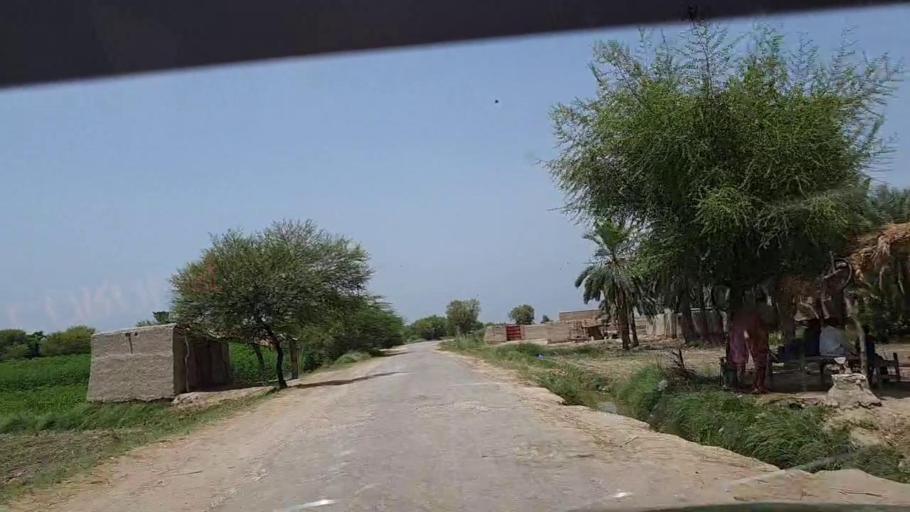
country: PK
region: Sindh
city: Khanpur
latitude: 27.7994
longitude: 69.4517
